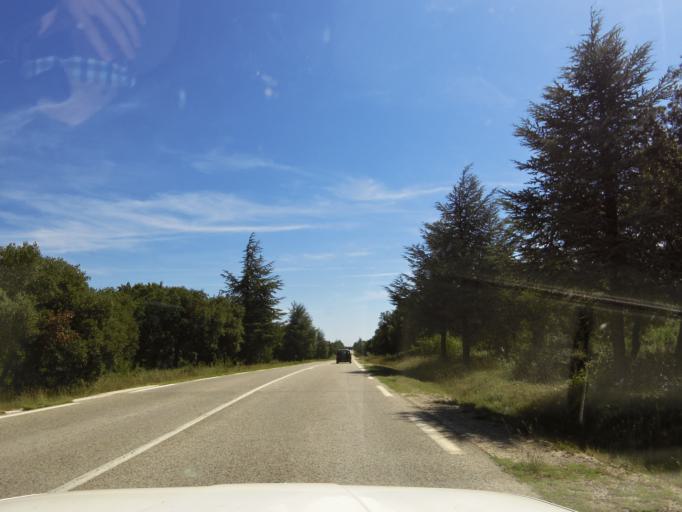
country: FR
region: Languedoc-Roussillon
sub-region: Departement du Gard
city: Saint-Quentin-la-Poterie
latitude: 44.1280
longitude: 4.4472
